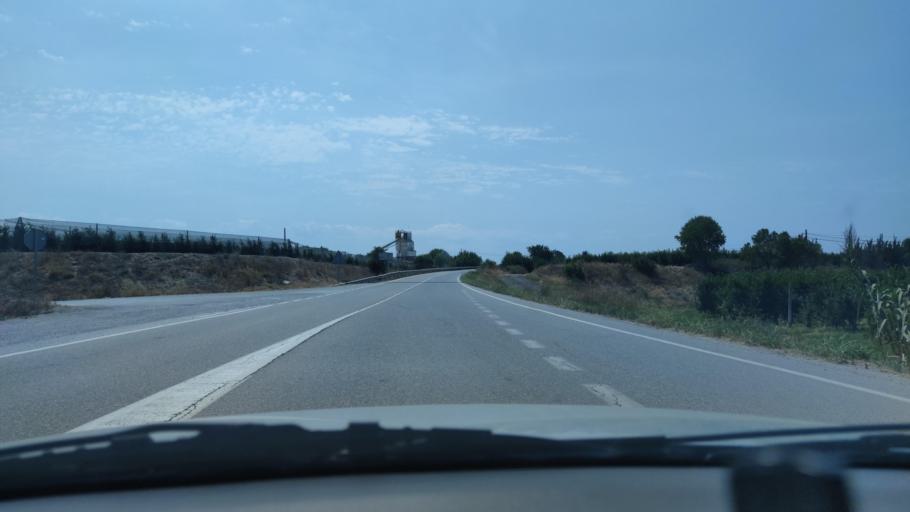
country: ES
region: Catalonia
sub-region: Provincia de Lleida
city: Bellpuig
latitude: 41.6432
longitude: 1.0010
